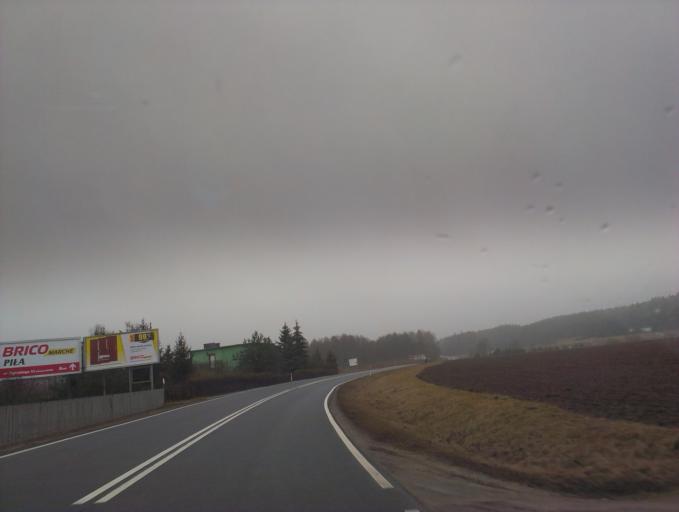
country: PL
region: Greater Poland Voivodeship
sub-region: Powiat pilski
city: Pila
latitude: 53.2156
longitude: 16.7860
